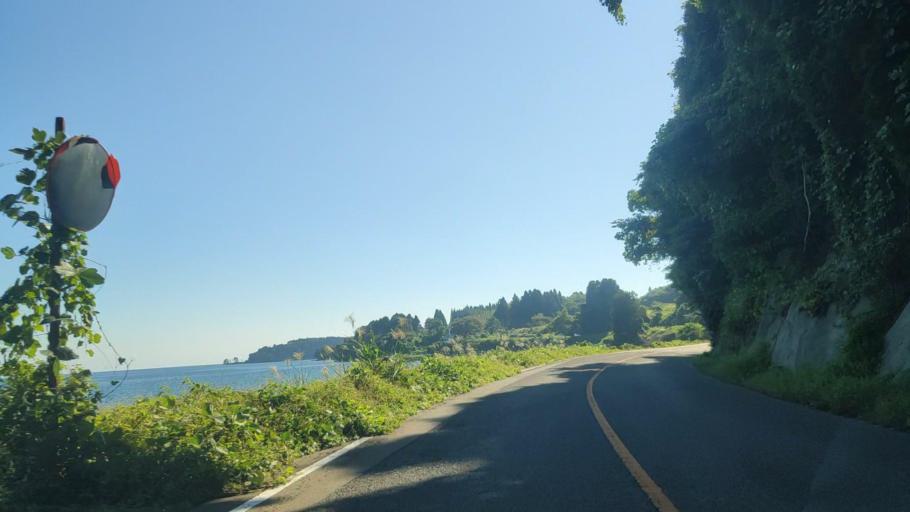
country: JP
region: Ishikawa
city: Nanao
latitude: 37.2727
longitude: 137.0968
